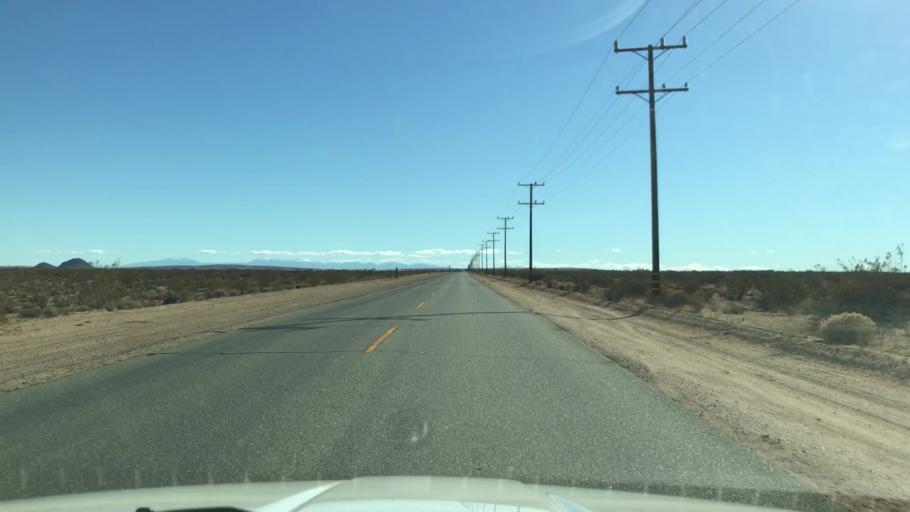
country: US
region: California
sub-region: Kern County
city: California City
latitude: 35.1742
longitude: -117.9858
